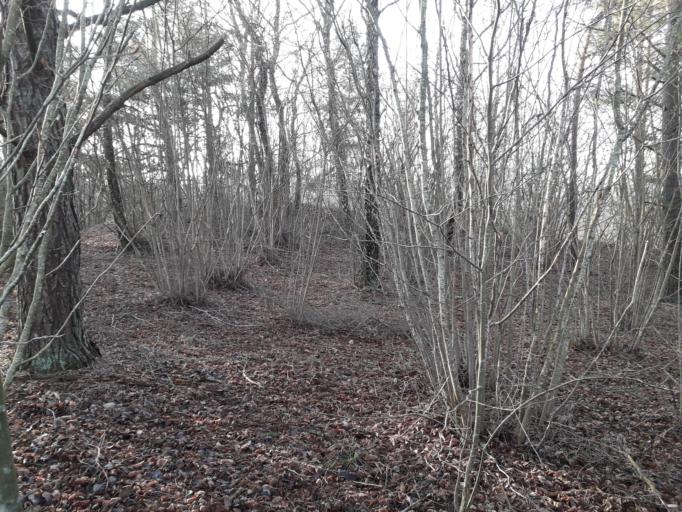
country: LT
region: Alytaus apskritis
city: Druskininkai
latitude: 54.1289
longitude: 24.0419
